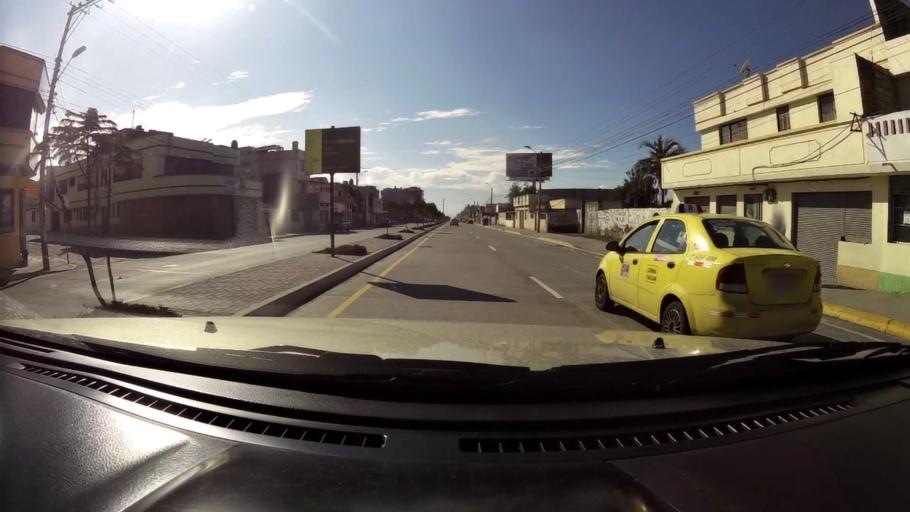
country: EC
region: Chimborazo
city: Riobamba
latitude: -1.6479
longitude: -78.6713
